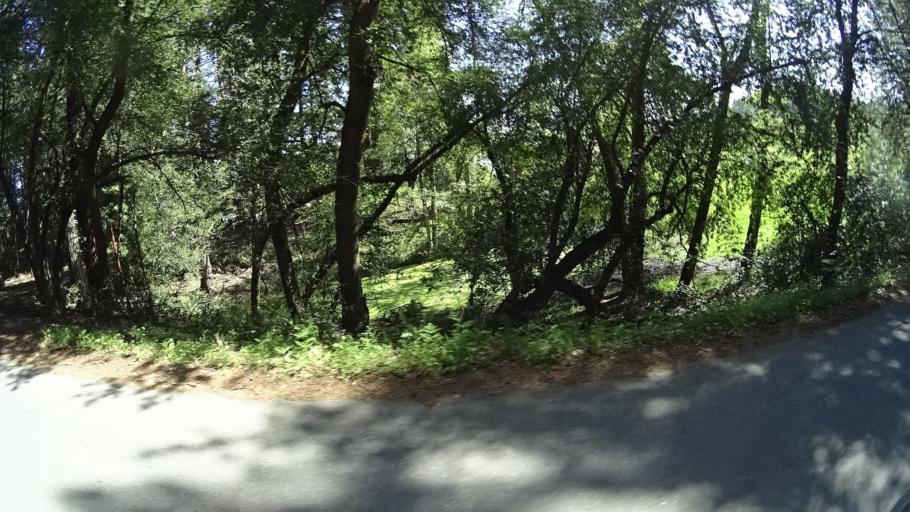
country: US
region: California
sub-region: Humboldt County
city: Redway
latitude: 40.0849
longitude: -123.6611
